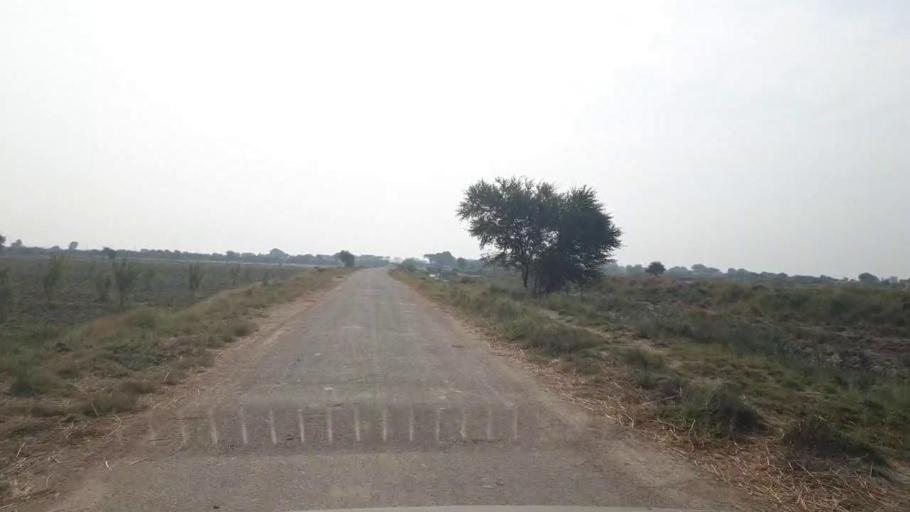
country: PK
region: Sindh
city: Tando Muhammad Khan
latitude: 25.1216
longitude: 68.5004
